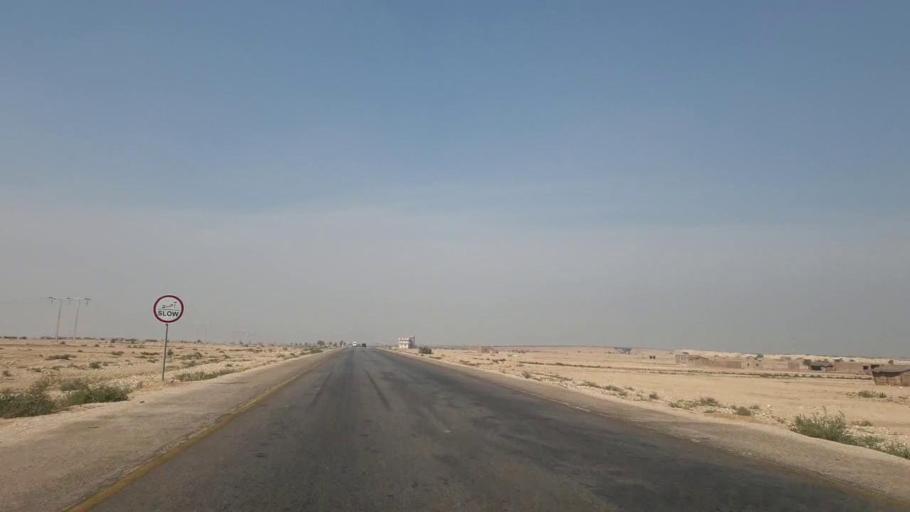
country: PK
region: Sindh
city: Hala
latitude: 25.8495
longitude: 68.2602
